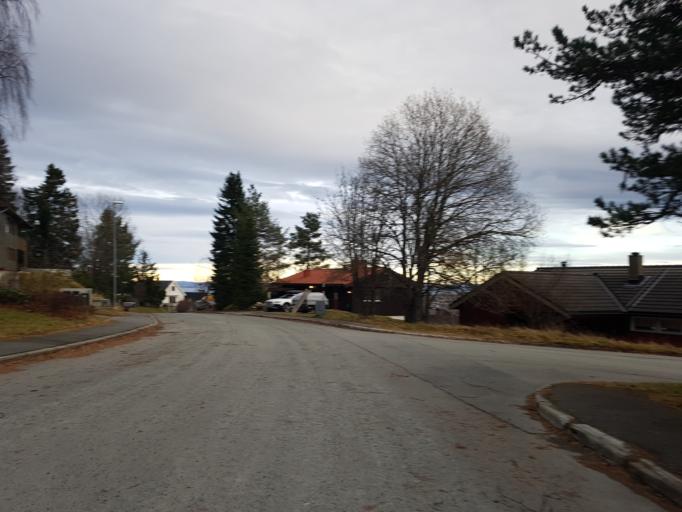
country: NO
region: Sor-Trondelag
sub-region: Trondheim
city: Trondheim
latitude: 63.4092
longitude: 10.3465
